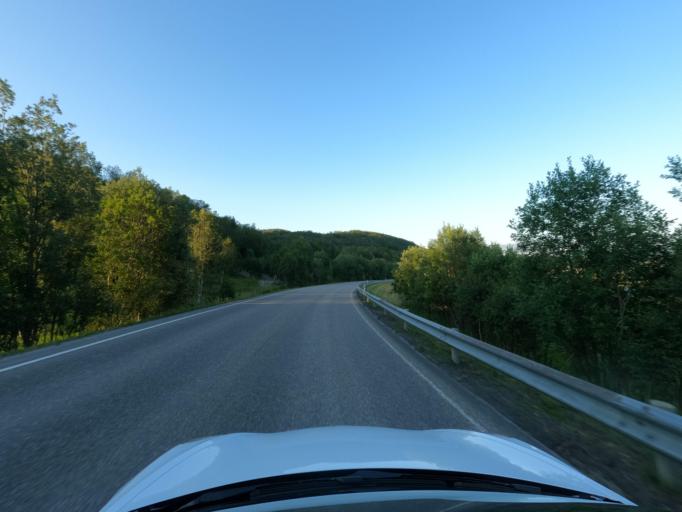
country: NO
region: Troms
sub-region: Harstad
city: Harstad
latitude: 68.7192
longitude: 16.5115
